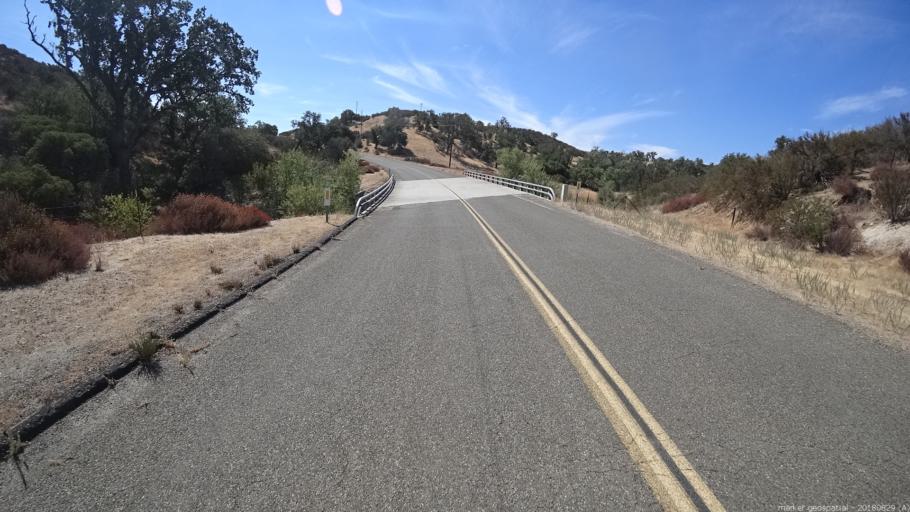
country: US
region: California
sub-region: San Luis Obispo County
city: Lake Nacimiento
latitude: 35.8085
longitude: -120.9818
